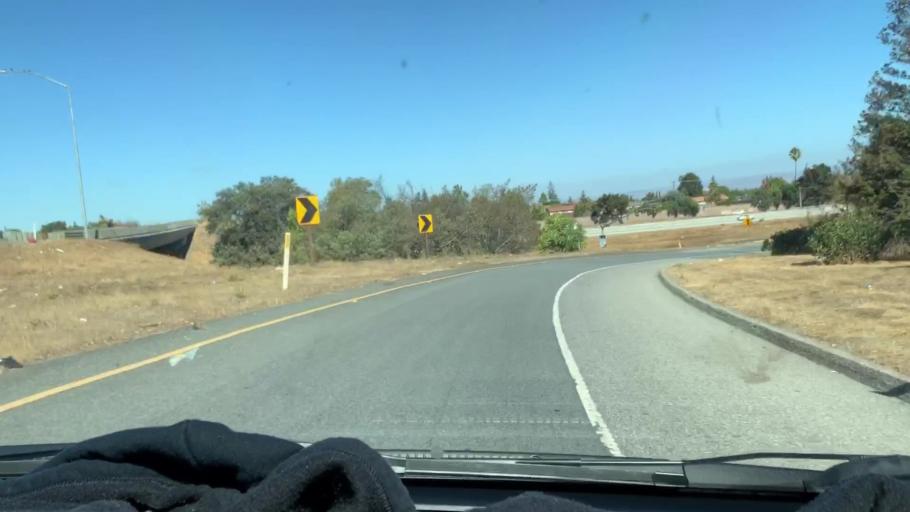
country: US
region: California
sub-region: Santa Clara County
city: Cupertino
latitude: 37.3311
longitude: -122.0527
